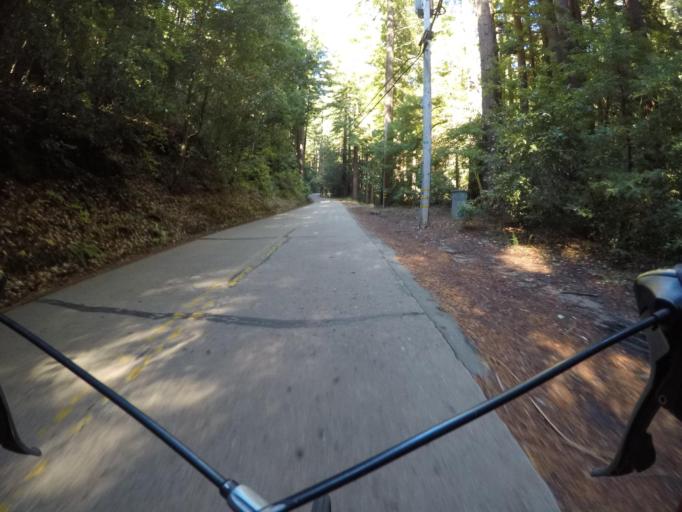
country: US
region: California
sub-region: Santa Clara County
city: Lexington Hills
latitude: 37.1180
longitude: -121.9865
